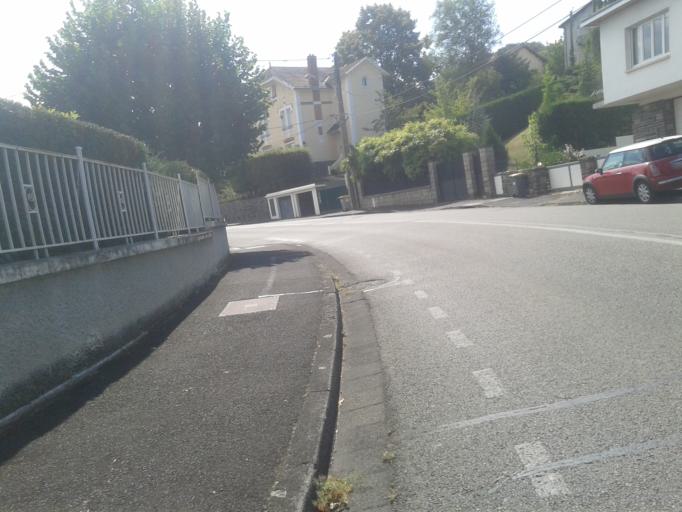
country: FR
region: Auvergne
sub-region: Departement du Puy-de-Dome
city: Chamalieres
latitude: 45.7741
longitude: 3.0536
